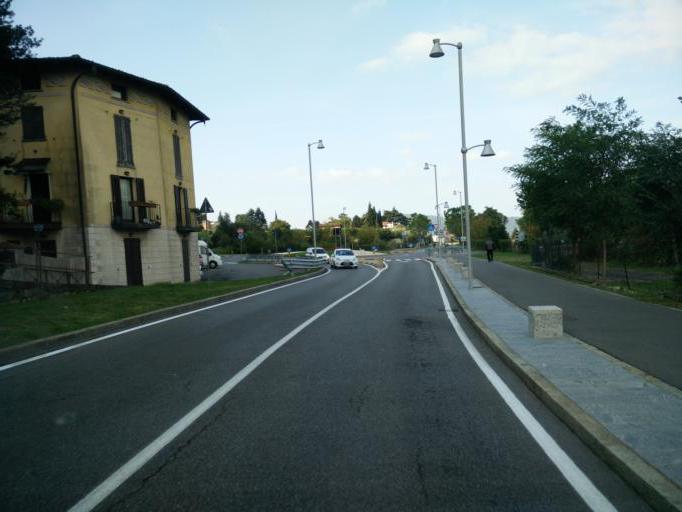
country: IT
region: Lombardy
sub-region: Provincia di Brescia
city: Iseo
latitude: 45.6657
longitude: 10.0661
